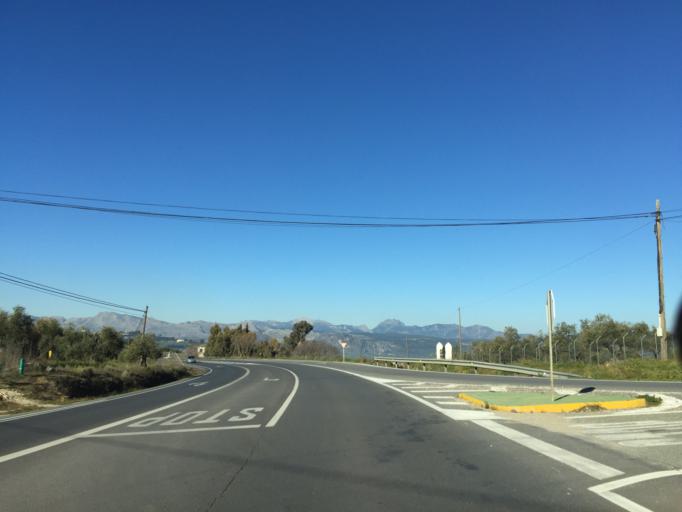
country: ES
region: Andalusia
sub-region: Provincia de Malaga
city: Arriate
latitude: 36.7639
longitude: -5.1355
